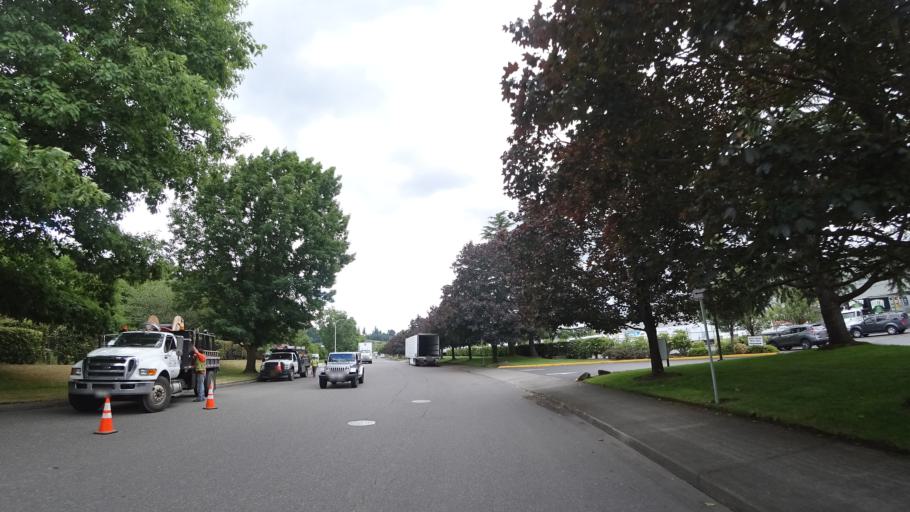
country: US
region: Oregon
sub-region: Multnomah County
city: Portland
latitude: 45.5706
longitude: -122.7087
